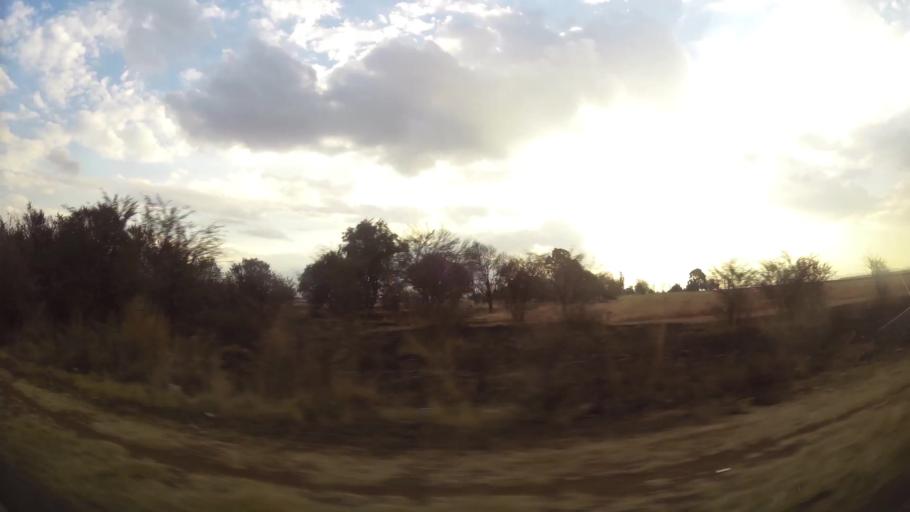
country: ZA
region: Gauteng
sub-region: Sedibeng District Municipality
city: Vanderbijlpark
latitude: -26.6296
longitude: 27.8093
